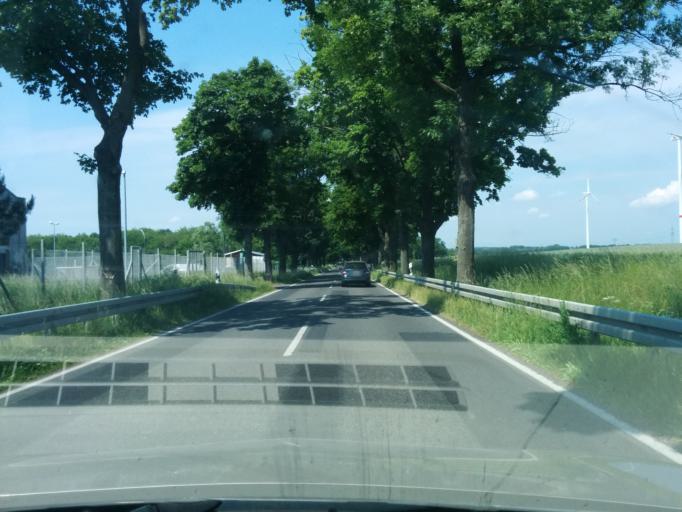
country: DE
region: Brandenburg
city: Ahrensfelde
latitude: 52.6114
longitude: 13.5958
